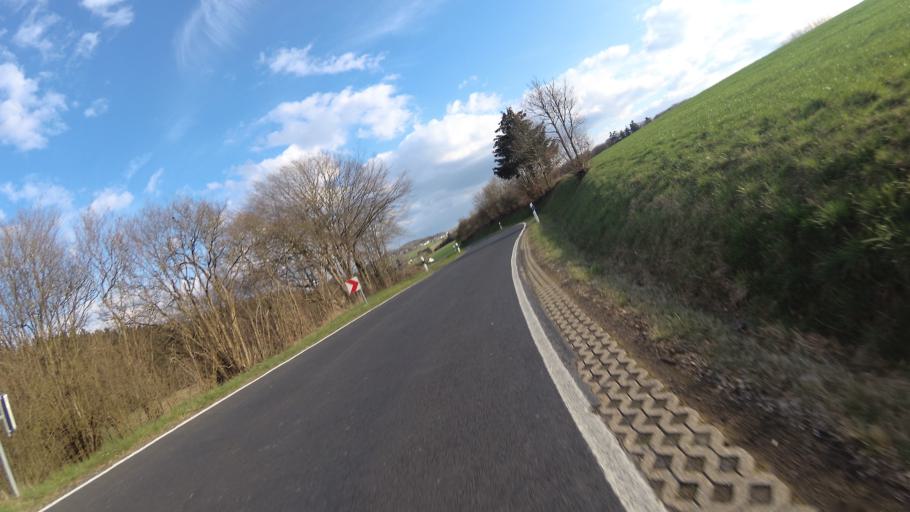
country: DE
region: Rheinland-Pfalz
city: Steiningen
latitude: 50.1956
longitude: 6.9025
